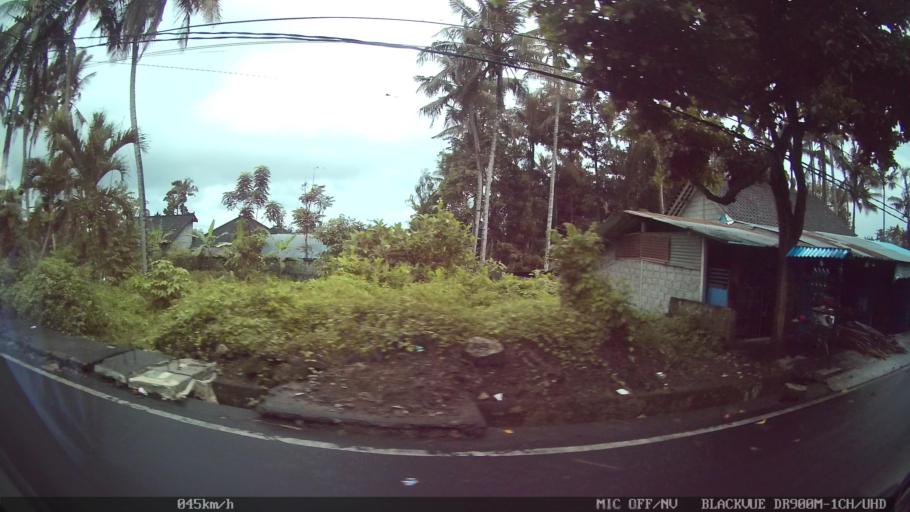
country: ID
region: Bali
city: Pegongan
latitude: -8.4888
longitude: 115.2395
